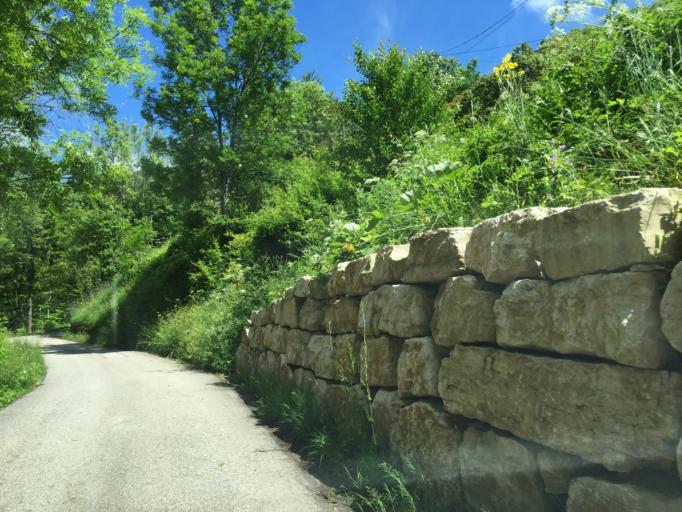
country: FR
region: Rhone-Alpes
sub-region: Departement de la Savoie
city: Vimines
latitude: 45.4734
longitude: 5.8934
